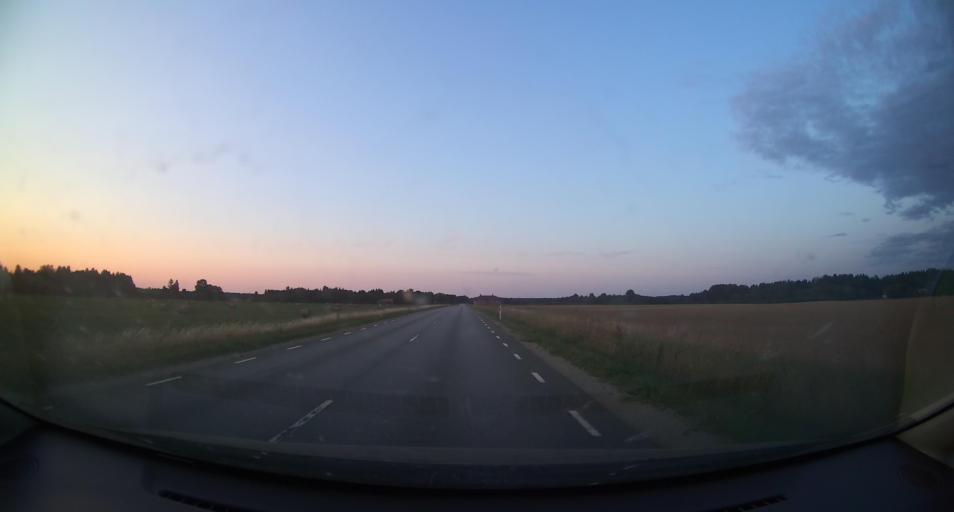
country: EE
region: Harju
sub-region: Anija vald
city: Kehra
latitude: 59.2755
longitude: 25.3582
